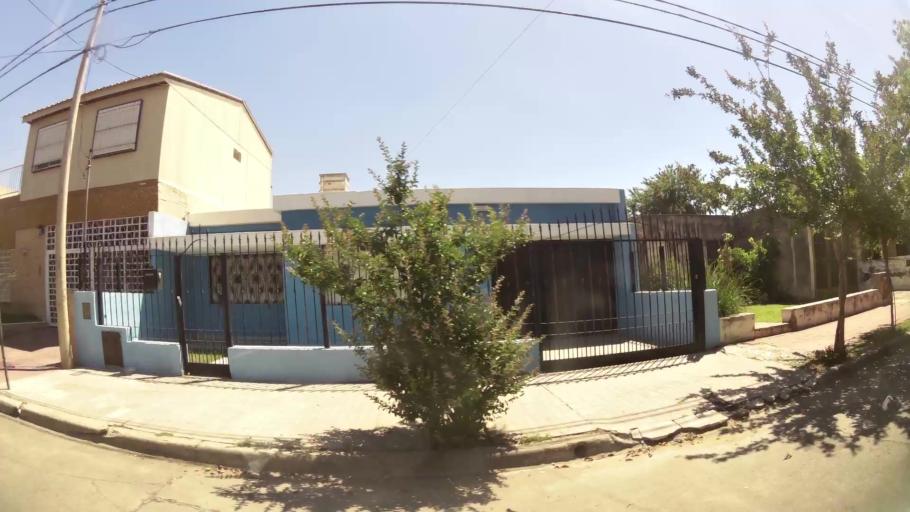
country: AR
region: Cordoba
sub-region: Departamento de Capital
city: Cordoba
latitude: -31.3818
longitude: -64.1705
